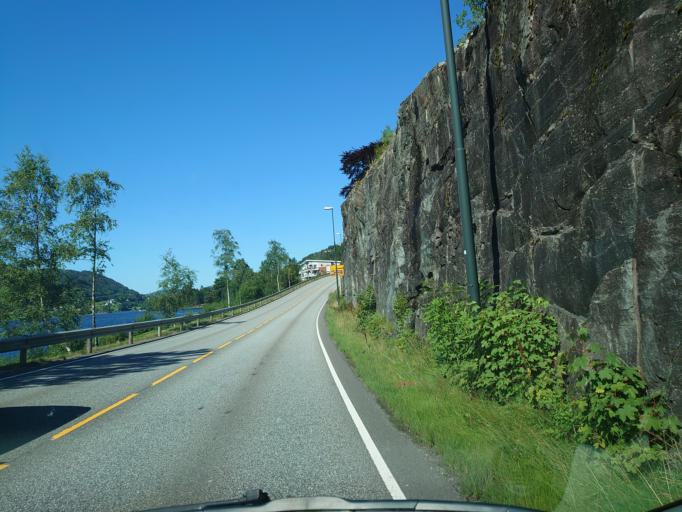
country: NO
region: Hordaland
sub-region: Bergen
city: Indre Arna
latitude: 60.4243
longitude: 5.4679
